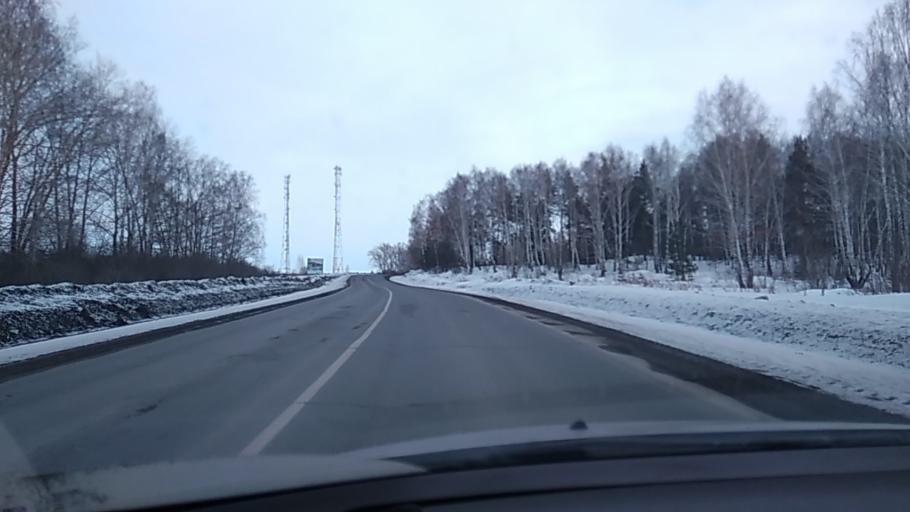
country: RU
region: Sverdlovsk
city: Dvurechensk
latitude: 56.6433
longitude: 61.2177
